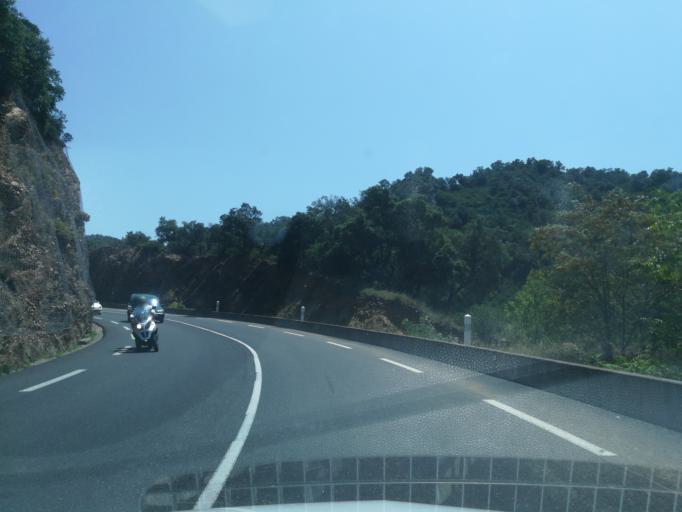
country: FR
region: Languedoc-Roussillon
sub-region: Departement des Pyrenees-Orientales
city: Maureillas-las-Illas
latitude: 42.4719
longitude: 2.8529
